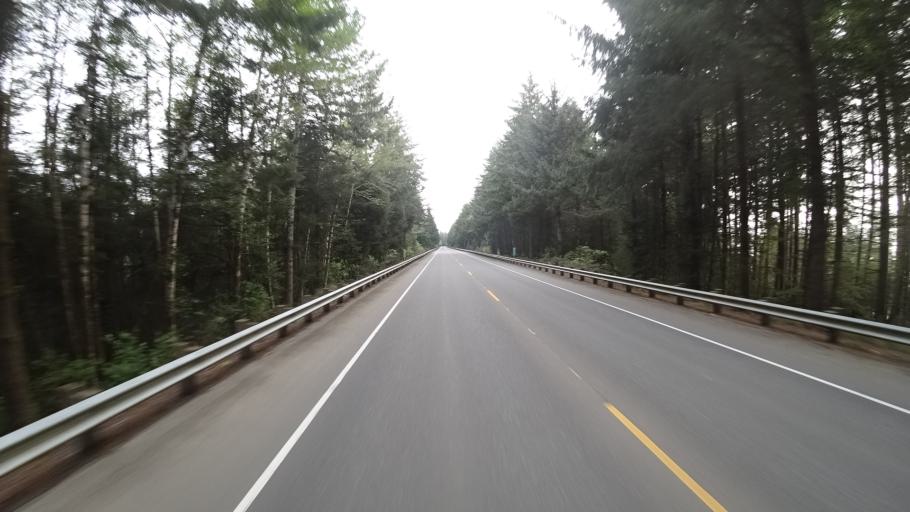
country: US
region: Oregon
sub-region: Coos County
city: Barview
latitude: 43.2450
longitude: -124.2876
